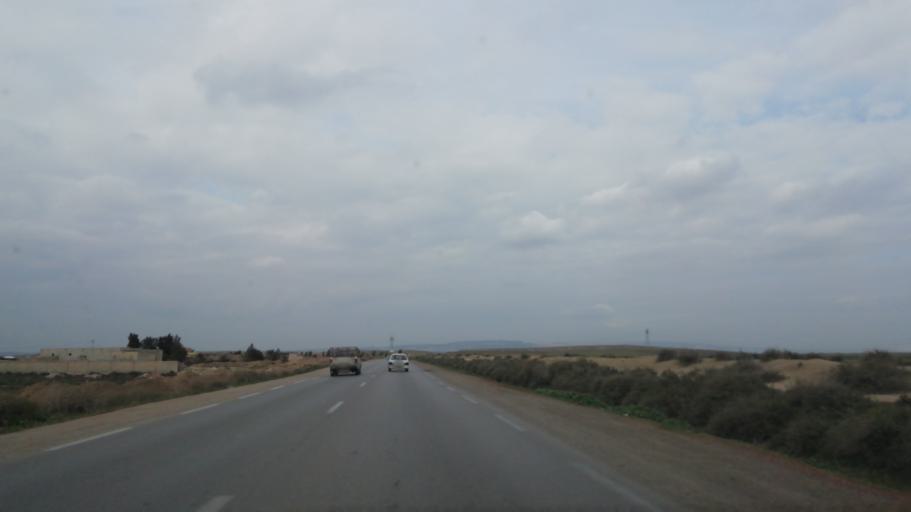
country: DZ
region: Mostaganem
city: Mostaganem
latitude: 35.7037
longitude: 0.0549
